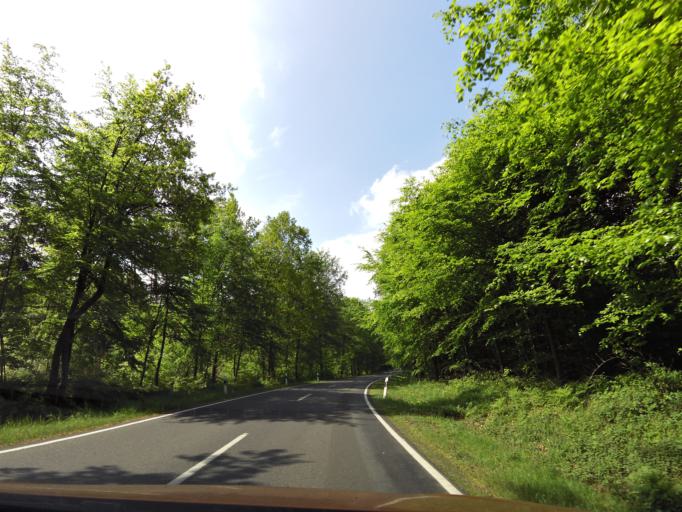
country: DE
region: Brandenburg
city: Gorzke
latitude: 52.0834
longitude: 12.3268
